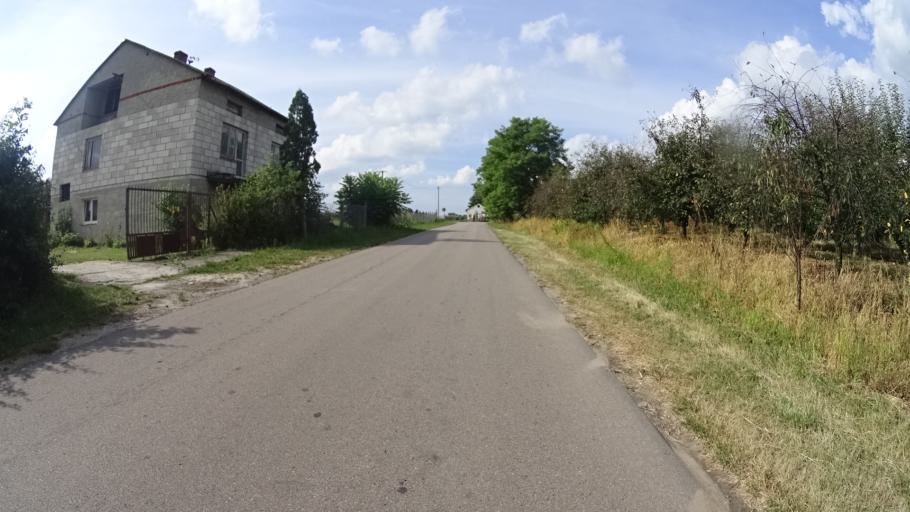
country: PL
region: Masovian Voivodeship
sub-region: Powiat grojecki
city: Goszczyn
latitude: 51.7004
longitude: 20.8470
